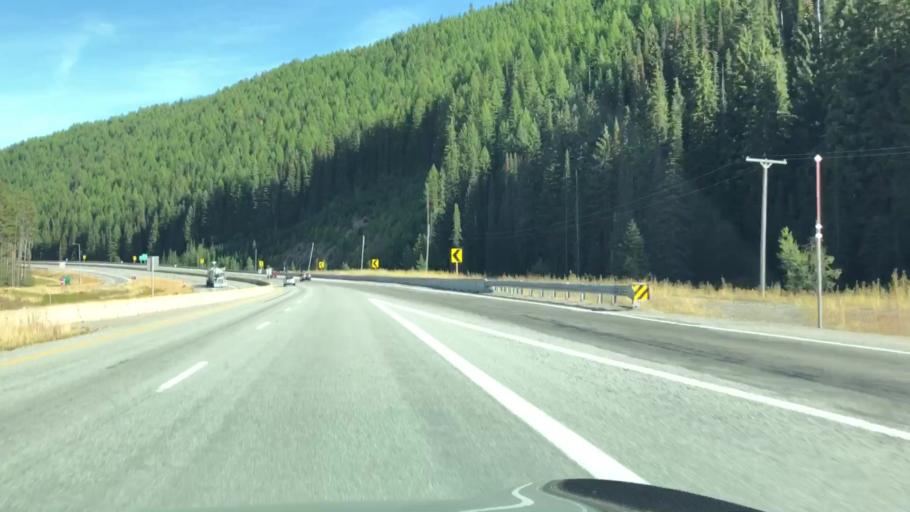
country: US
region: Idaho
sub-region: Shoshone County
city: Wallace
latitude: 47.4188
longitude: -115.6247
